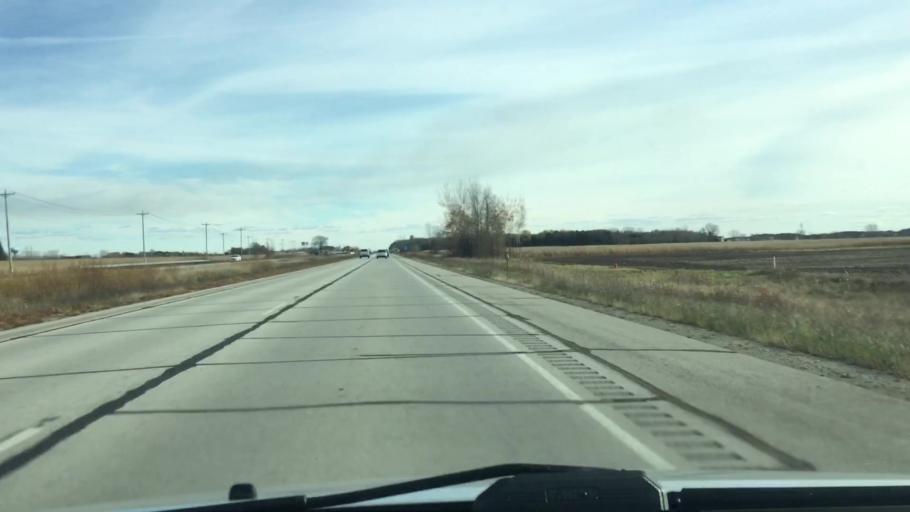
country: US
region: Wisconsin
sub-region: Brown County
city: Oneida
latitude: 44.5790
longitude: -88.1788
